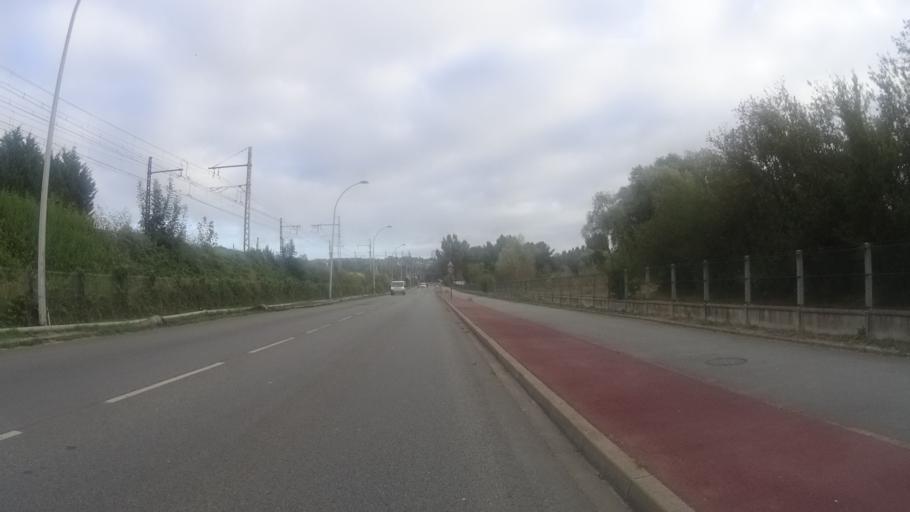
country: FR
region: Ile-de-France
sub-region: Departement de l'Essonne
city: Villabe
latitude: 48.5986
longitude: 2.4597
